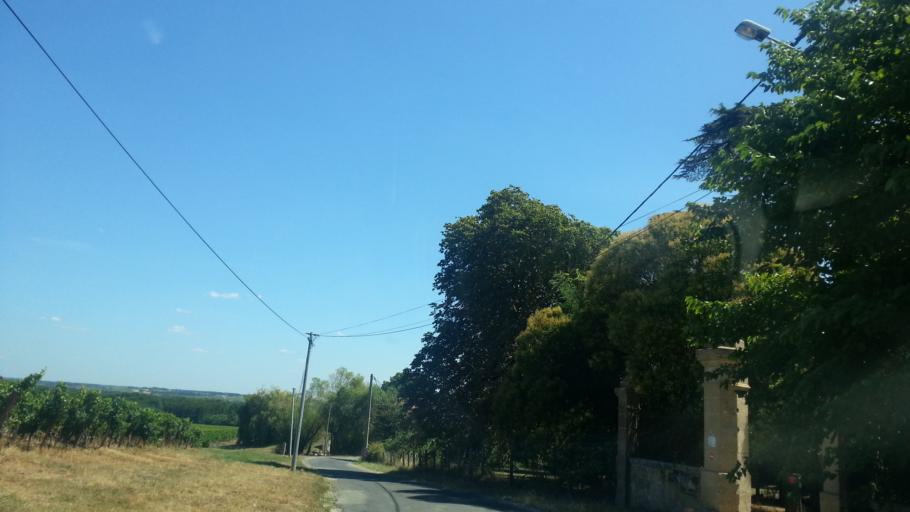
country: FR
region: Aquitaine
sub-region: Departement de la Gironde
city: Landiras
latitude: 44.5778
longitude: -0.3948
